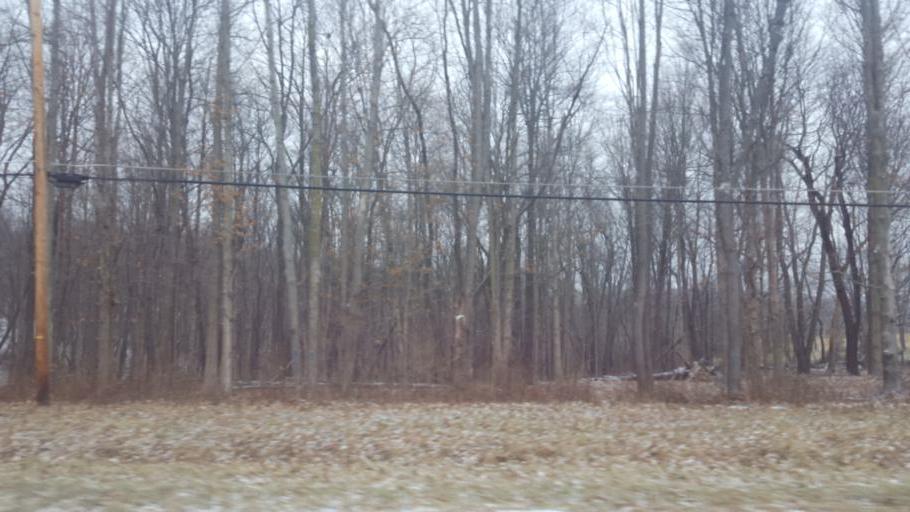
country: US
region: Ohio
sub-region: Knox County
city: Gambier
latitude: 40.3846
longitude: -82.4336
